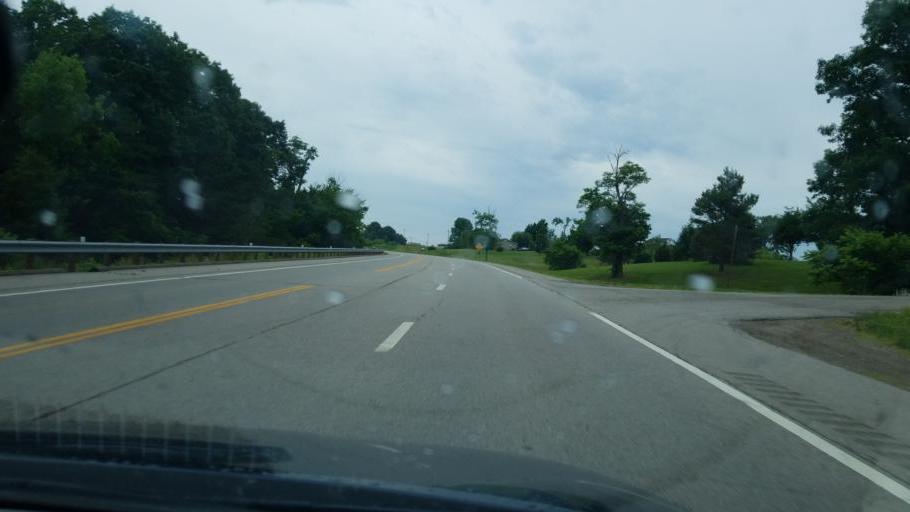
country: US
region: West Virginia
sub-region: Wood County
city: Washington
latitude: 39.2082
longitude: -81.8229
